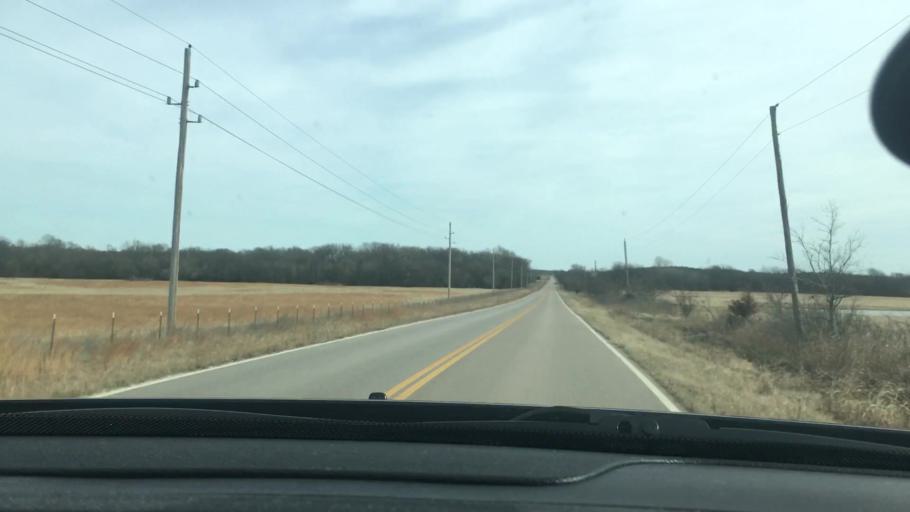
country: US
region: Oklahoma
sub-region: Murray County
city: Sulphur
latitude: 34.4036
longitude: -96.8707
